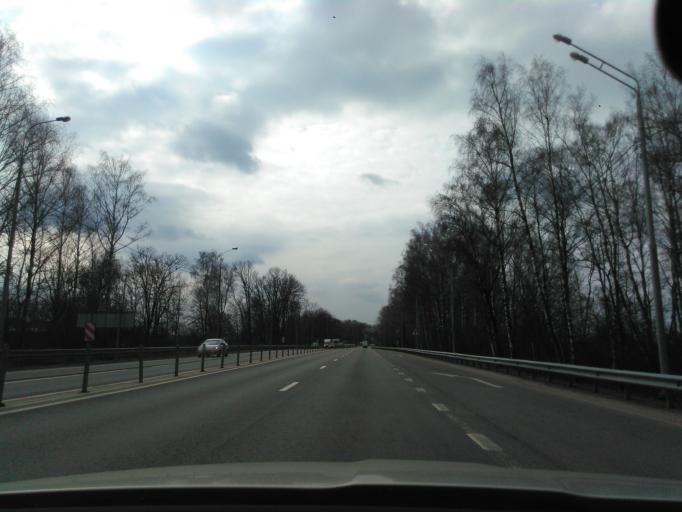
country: RU
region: Moskovskaya
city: Marfino
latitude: 56.0181
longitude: 37.5453
